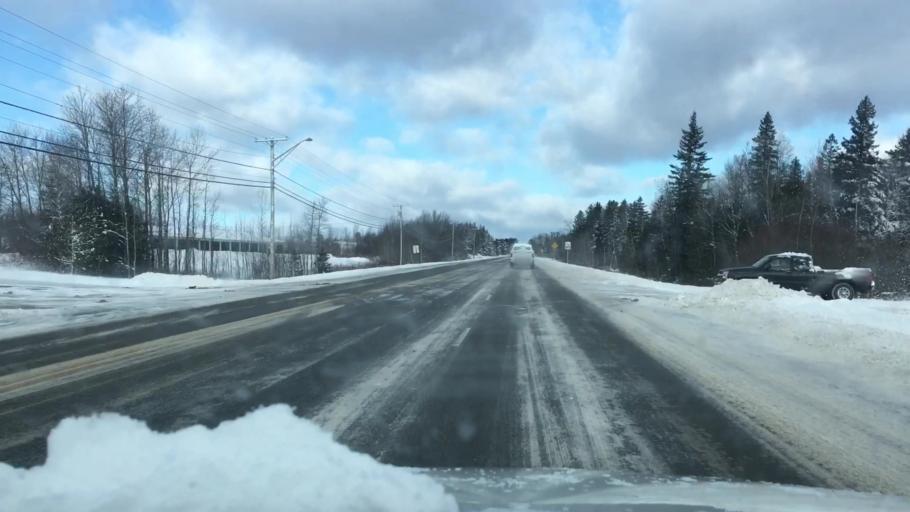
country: US
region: Maine
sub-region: Aroostook County
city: Caribou
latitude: 46.8736
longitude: -68.0031
